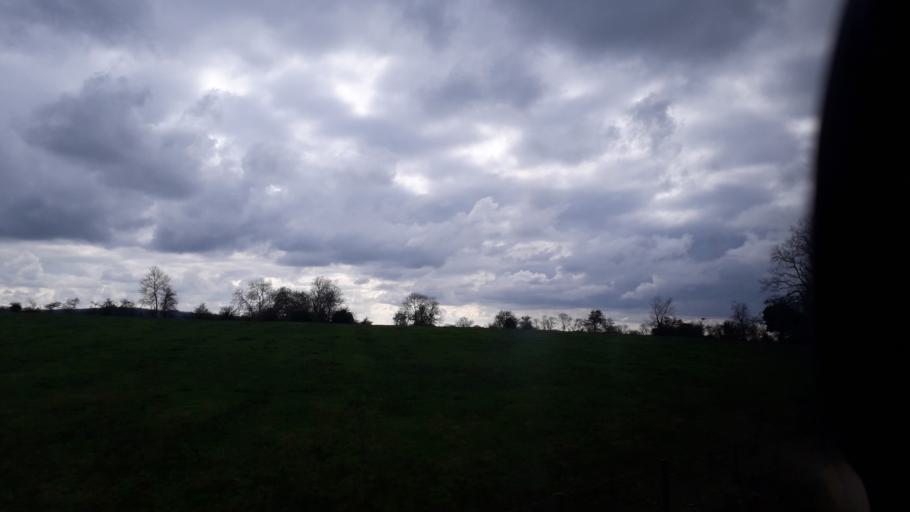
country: IE
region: Leinster
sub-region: An Longfort
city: Edgeworthstown
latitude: 53.7010
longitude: -7.6873
